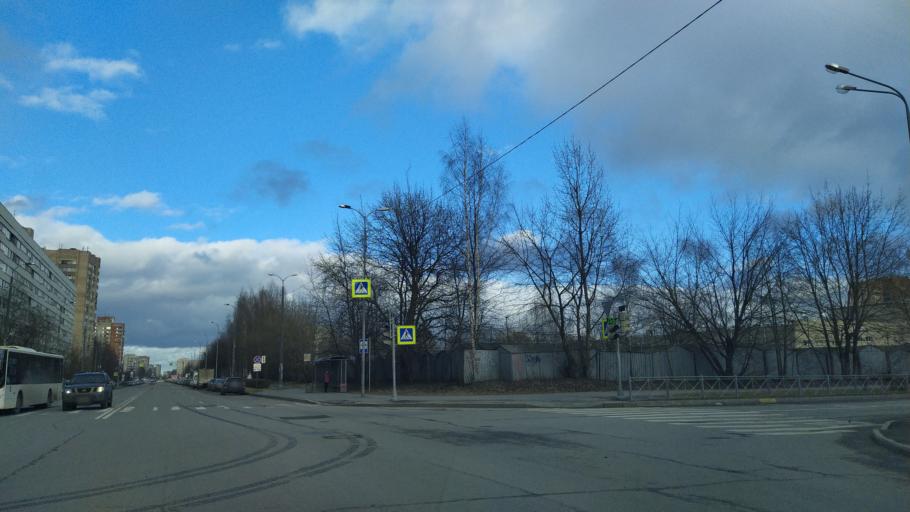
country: RU
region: St.-Petersburg
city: Grazhdanka
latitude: 60.0364
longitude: 30.3817
